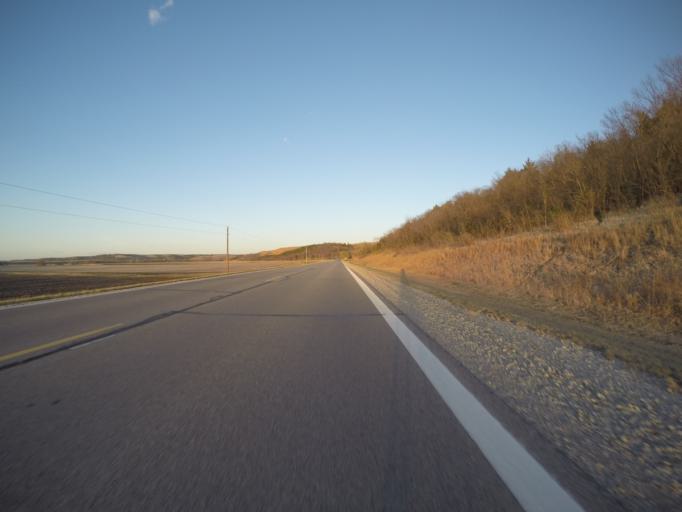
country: US
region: Kansas
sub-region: Riley County
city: Manhattan
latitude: 39.1176
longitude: -96.5860
